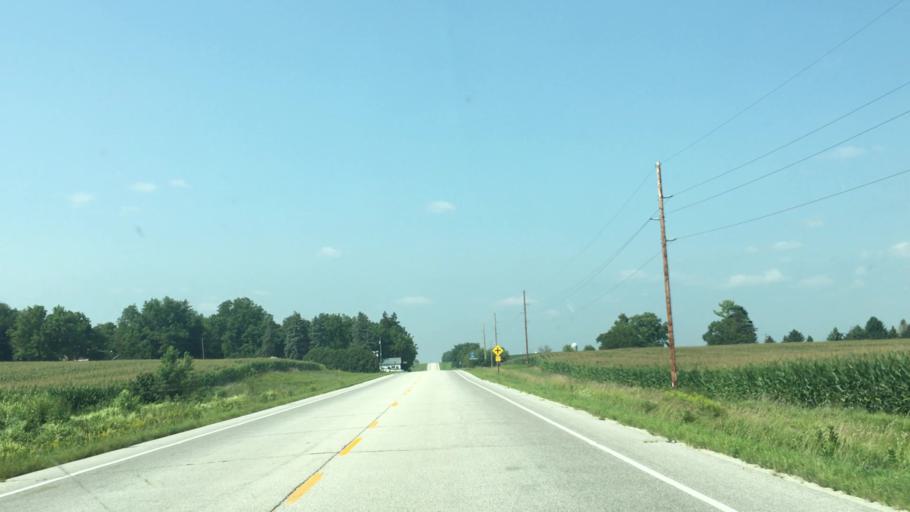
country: US
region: Minnesota
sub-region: Fillmore County
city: Harmony
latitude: 43.5916
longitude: -91.9298
